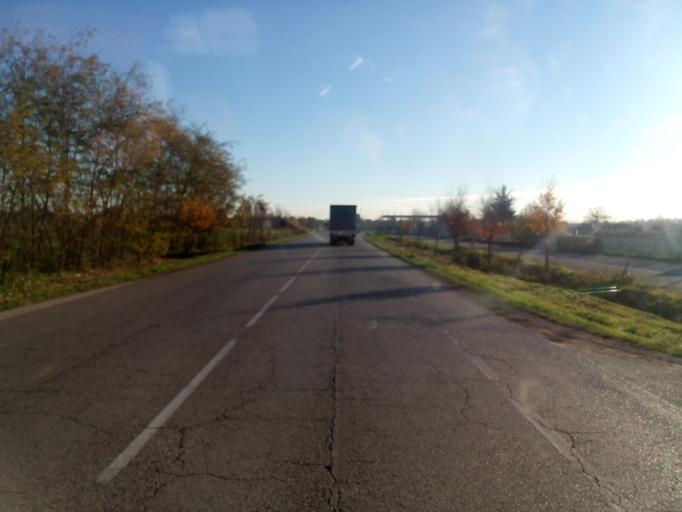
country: IT
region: Veneto
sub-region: Provincia di Vicenza
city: Sarcedo
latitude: 45.6940
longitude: 11.5069
